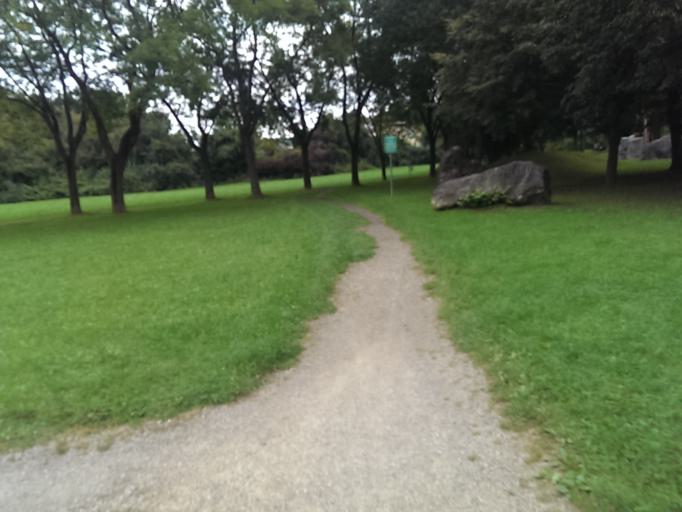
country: AT
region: Styria
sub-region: Graz Stadt
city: Graz
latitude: 47.0534
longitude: 15.4643
